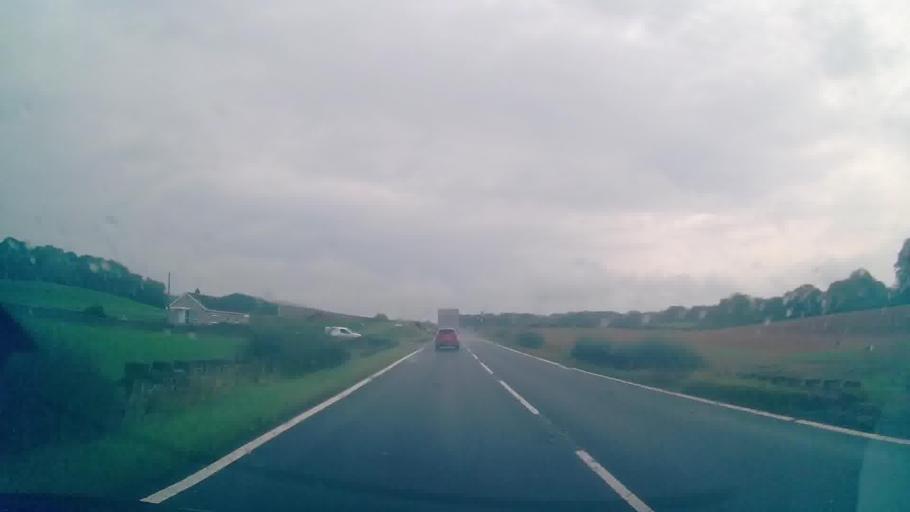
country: GB
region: Scotland
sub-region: Dumfries and Galloway
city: Lochmaben
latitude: 55.0441
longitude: -3.4486
